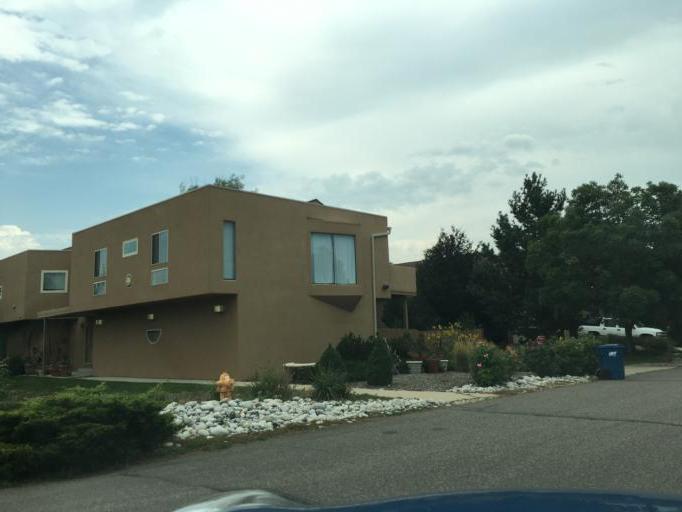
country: US
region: Colorado
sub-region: Jefferson County
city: Wheat Ridge
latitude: 39.7547
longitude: -105.1002
